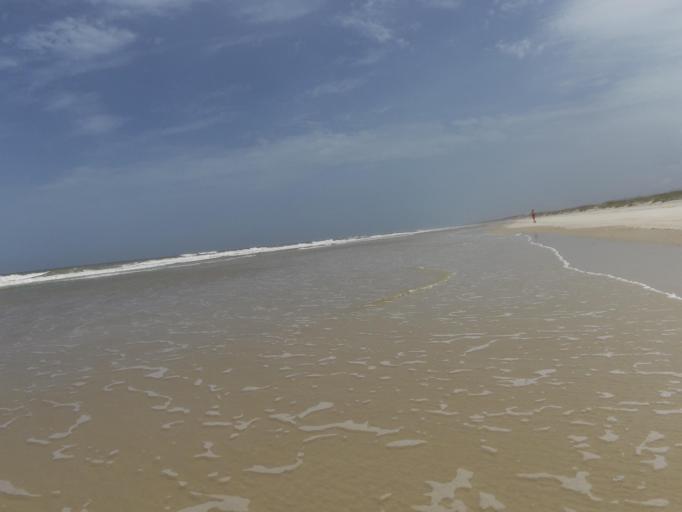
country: US
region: Florida
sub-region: Saint Johns County
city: Saint Augustine
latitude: 29.8969
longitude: -81.2761
